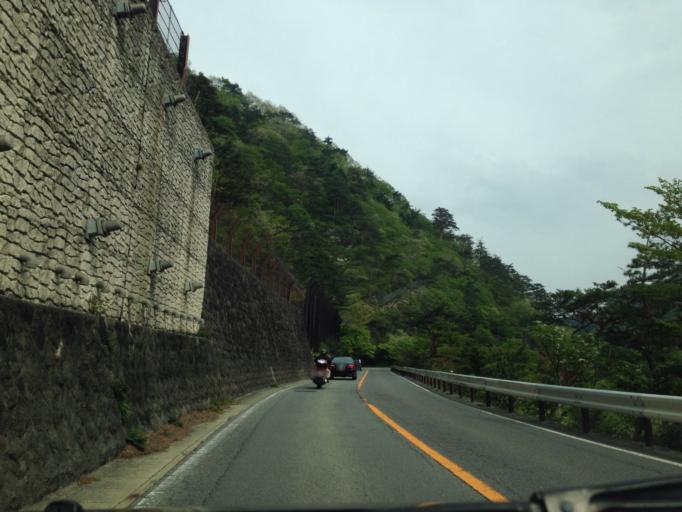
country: JP
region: Tochigi
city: Yaita
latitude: 36.9684
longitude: 139.8549
